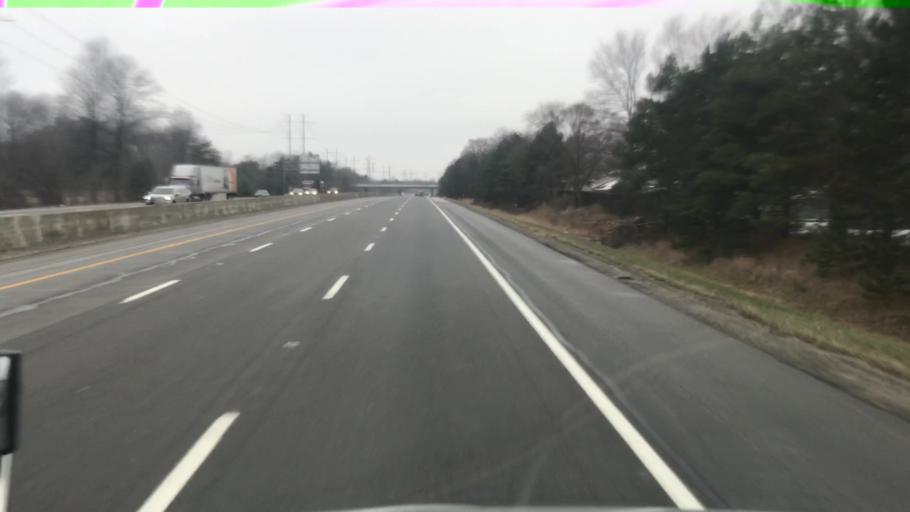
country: US
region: Ohio
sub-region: Cuyahoga County
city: Berea
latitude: 41.3452
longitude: -81.8518
